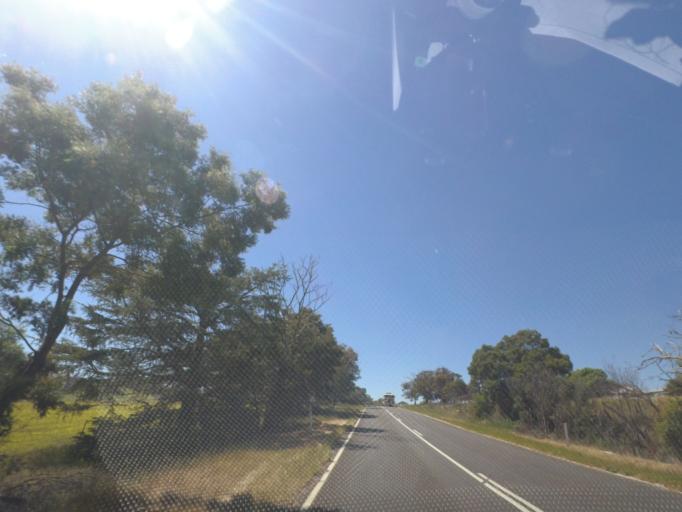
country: AU
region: Victoria
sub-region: Hume
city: Sunbury
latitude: -37.0767
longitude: 144.7700
